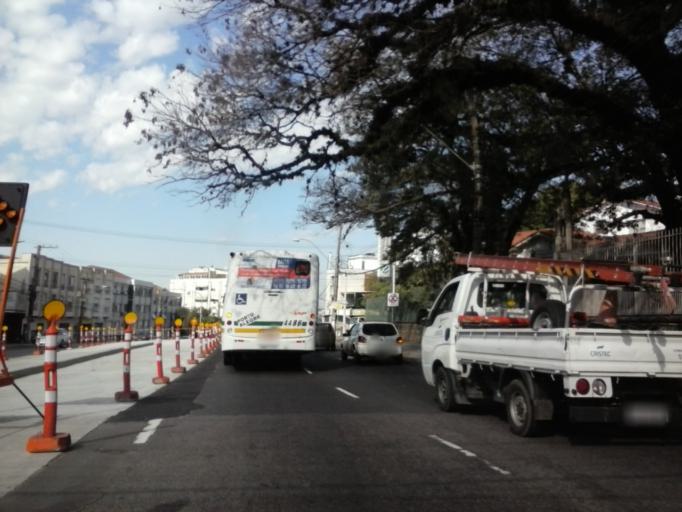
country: BR
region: Rio Grande do Sul
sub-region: Porto Alegre
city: Porto Alegre
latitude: -30.0394
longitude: -51.1723
